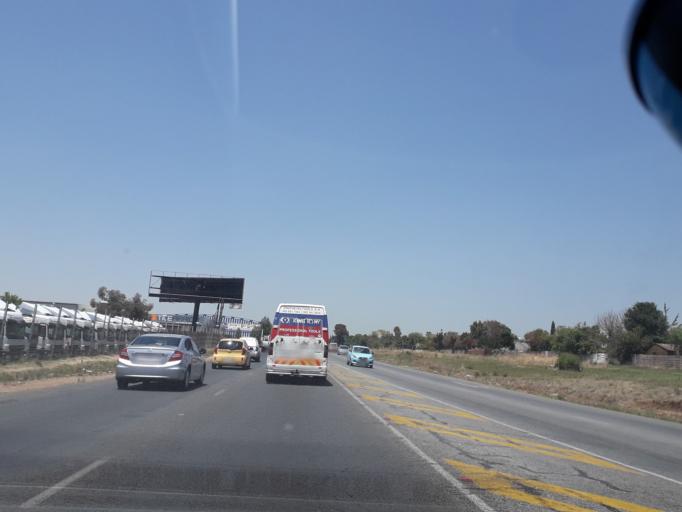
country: ZA
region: Gauteng
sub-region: City of Tshwane Metropolitan Municipality
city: Centurion
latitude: -25.8936
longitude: 28.1599
